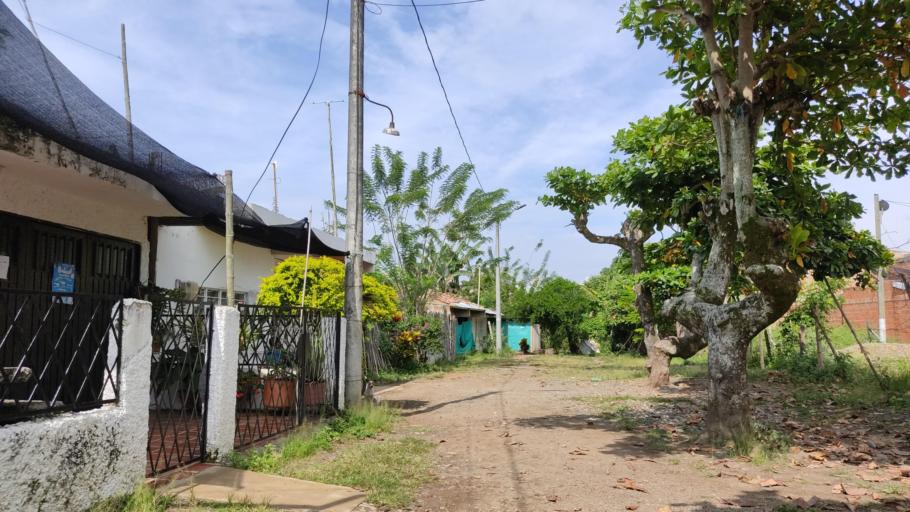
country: CO
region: Cauca
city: Buenos Aires
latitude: 3.1275
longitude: -76.5905
